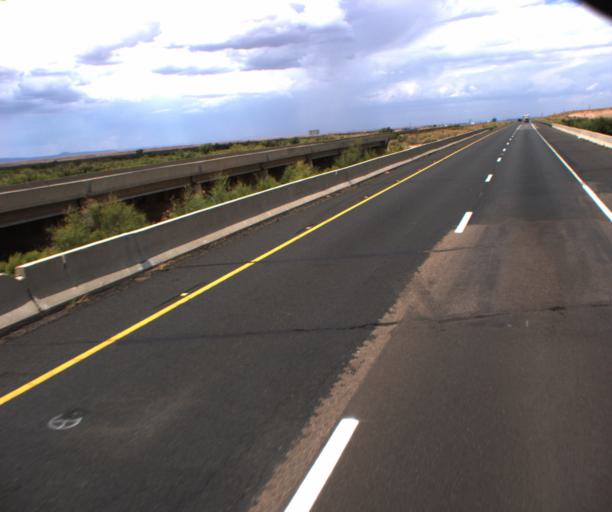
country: US
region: Arizona
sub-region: Navajo County
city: Winslow
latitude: 35.0040
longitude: -110.6094
